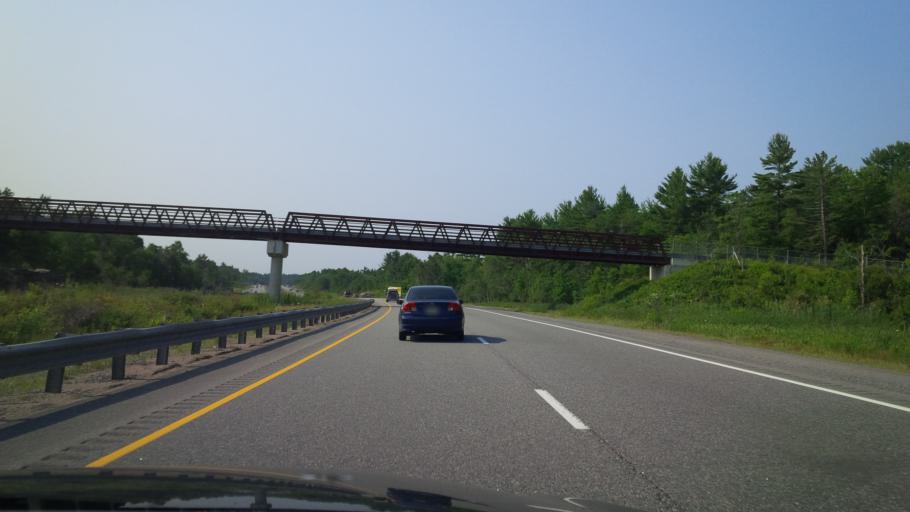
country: CA
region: Ontario
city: Gravenhurst
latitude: 44.9327
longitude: -79.3444
